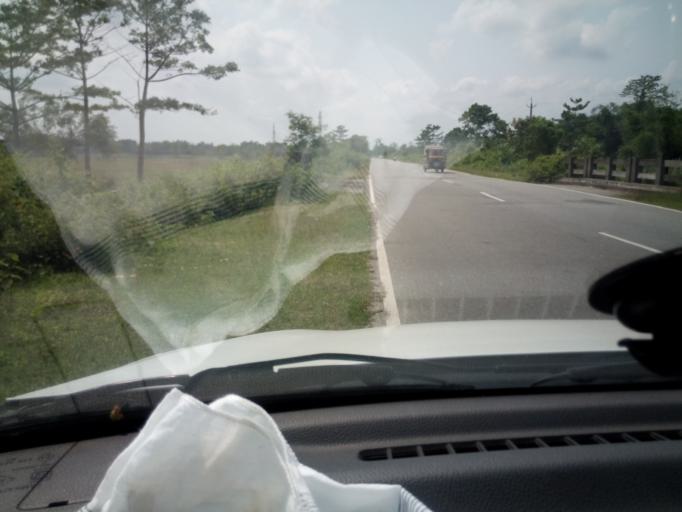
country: IN
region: Assam
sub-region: Udalguri
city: Udalguri
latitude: 26.7372
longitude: 92.1646
